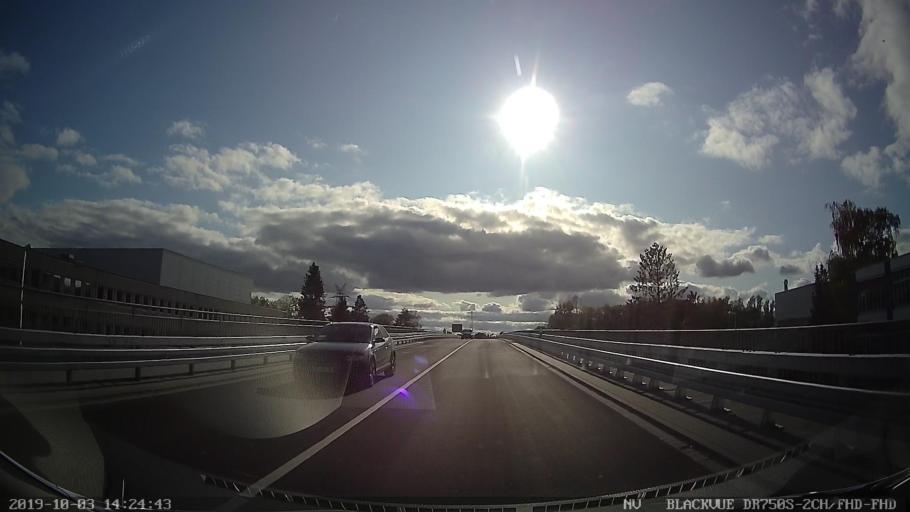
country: DE
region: Schleswig-Holstein
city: Pinneberg
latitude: 53.6683
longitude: 9.7782
